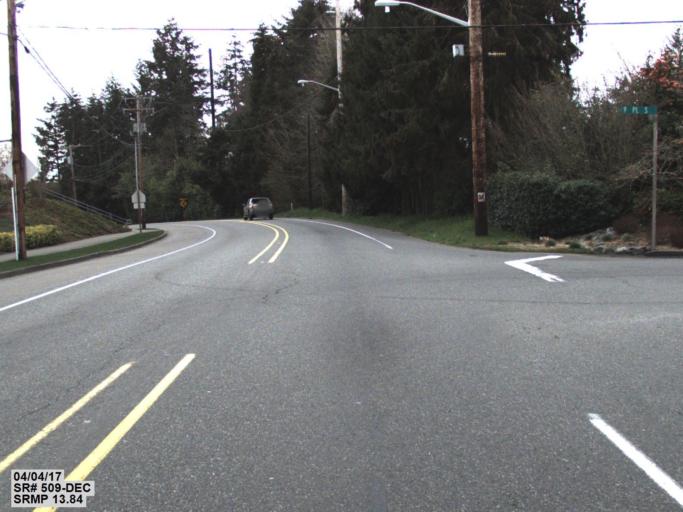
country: US
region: Washington
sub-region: King County
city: Federal Way
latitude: 47.3345
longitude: -122.3200
